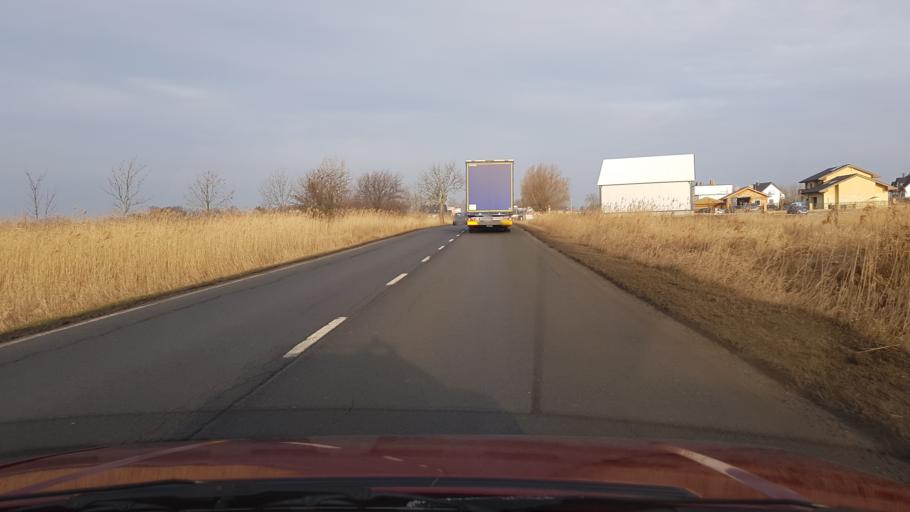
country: PL
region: West Pomeranian Voivodeship
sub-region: Powiat policki
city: Police
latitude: 53.5061
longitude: 14.5732
